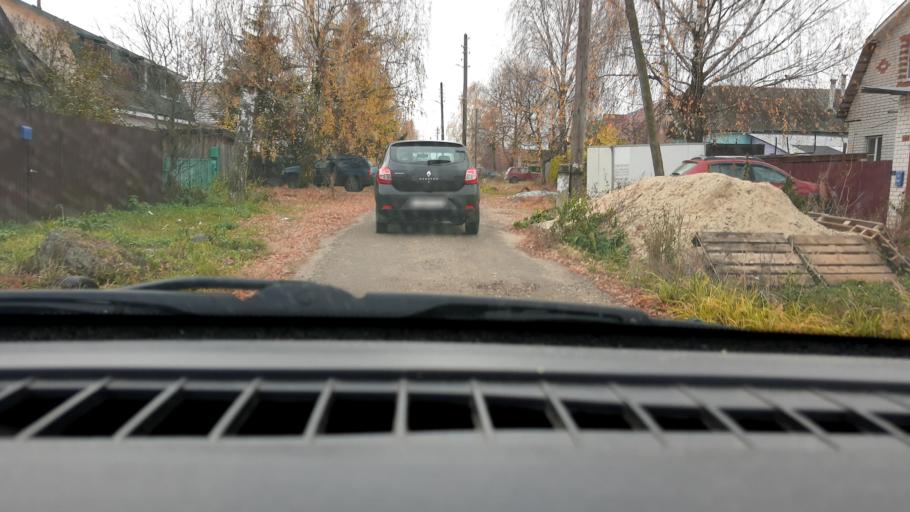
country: RU
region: Nizjnij Novgorod
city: Lukino
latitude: 56.4038
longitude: 43.7200
